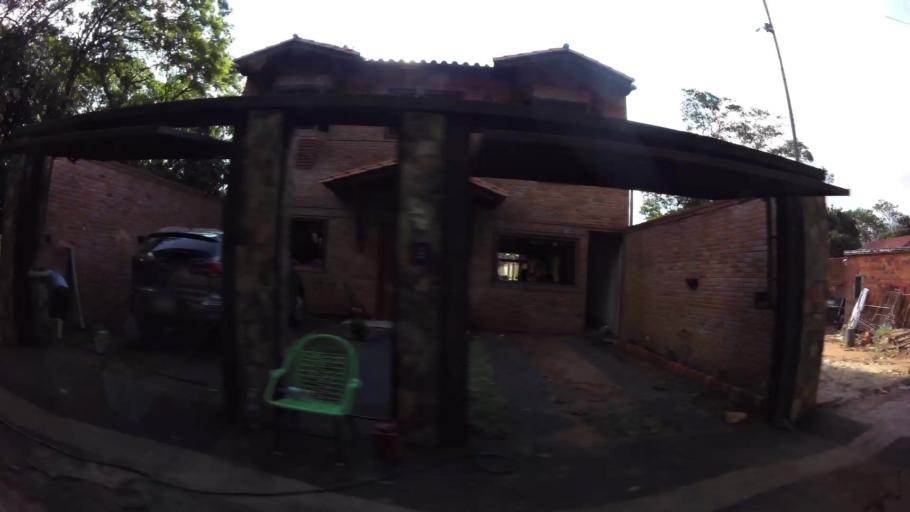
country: PY
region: Central
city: Fernando de la Mora
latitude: -25.3528
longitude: -57.5539
